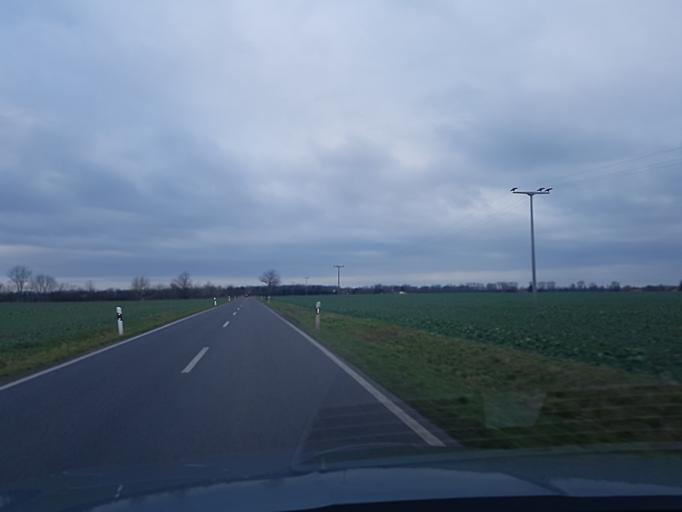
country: DE
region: Brandenburg
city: Sonnewalde
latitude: 51.6932
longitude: 13.6653
